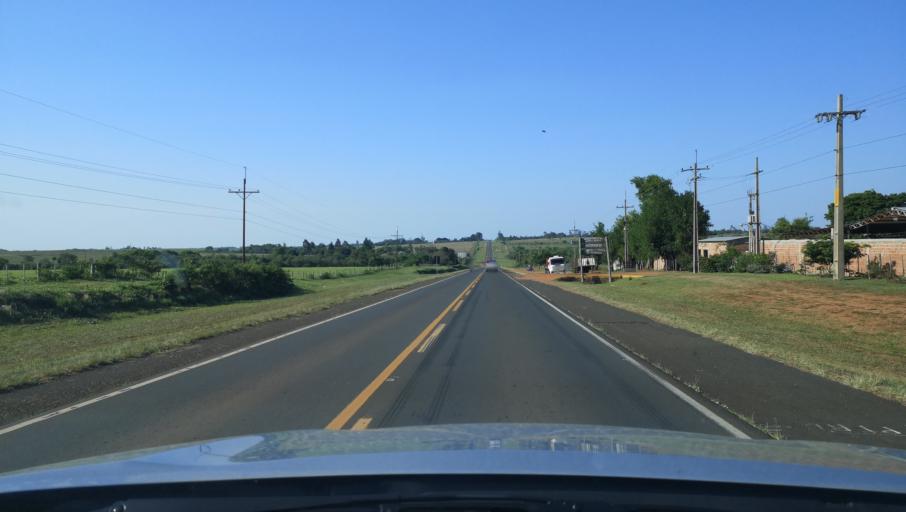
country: PY
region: Misiones
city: Santa Maria
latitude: -26.8377
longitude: -57.0346
